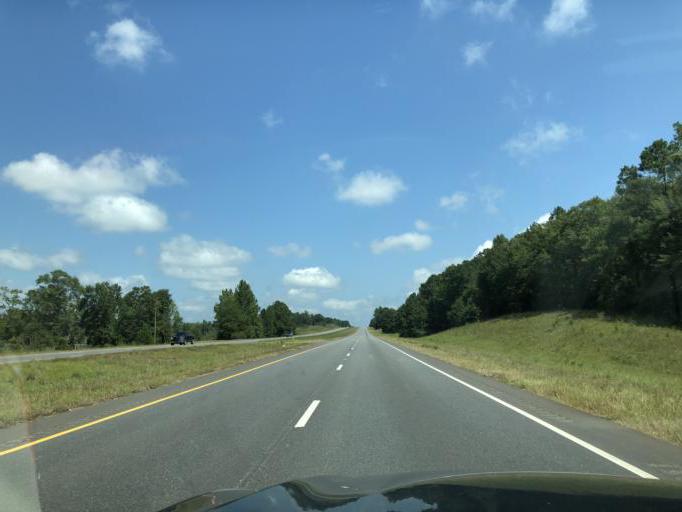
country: US
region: Alabama
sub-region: Henry County
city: Abbeville
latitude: 31.4711
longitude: -85.3037
